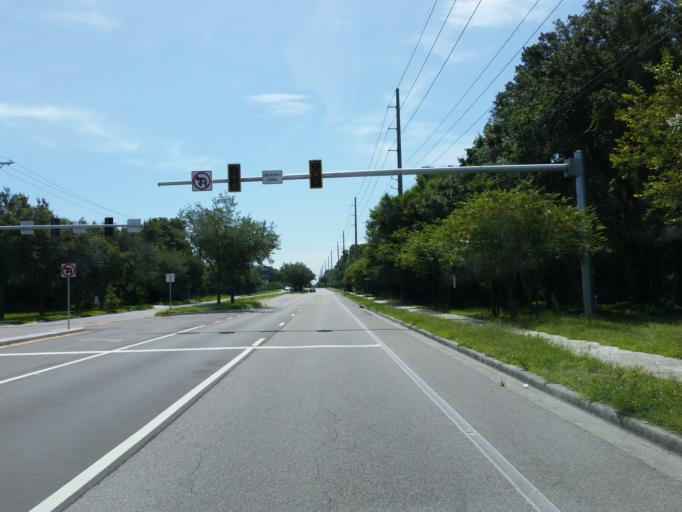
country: US
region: Florida
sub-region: Hillsborough County
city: Bloomingdale
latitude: 27.8936
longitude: -82.2620
